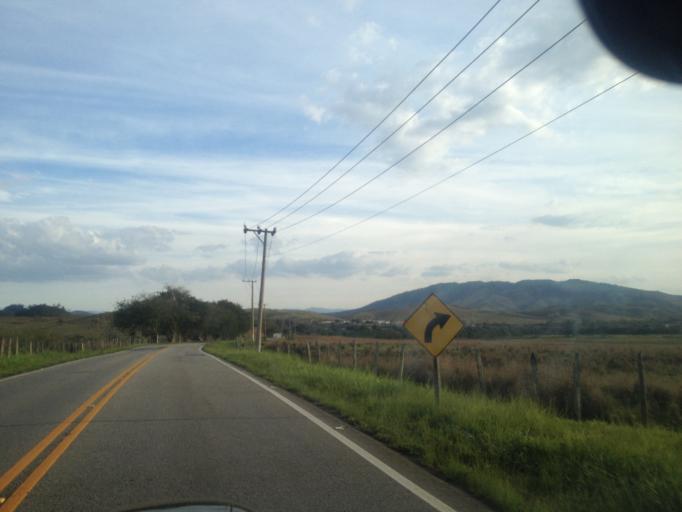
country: BR
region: Rio de Janeiro
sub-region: Porto Real
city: Porto Real
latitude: -22.4419
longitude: -44.2927
